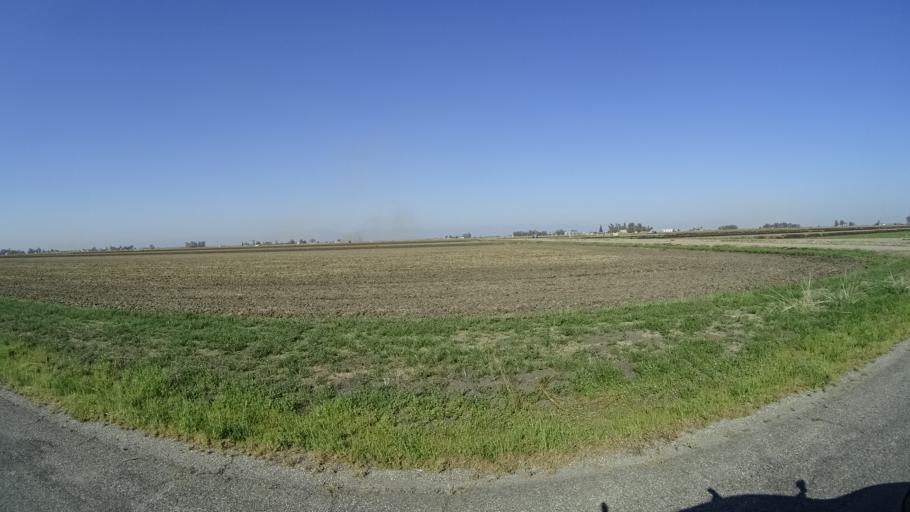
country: US
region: California
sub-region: Glenn County
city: Willows
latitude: 39.5685
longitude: -122.0839
